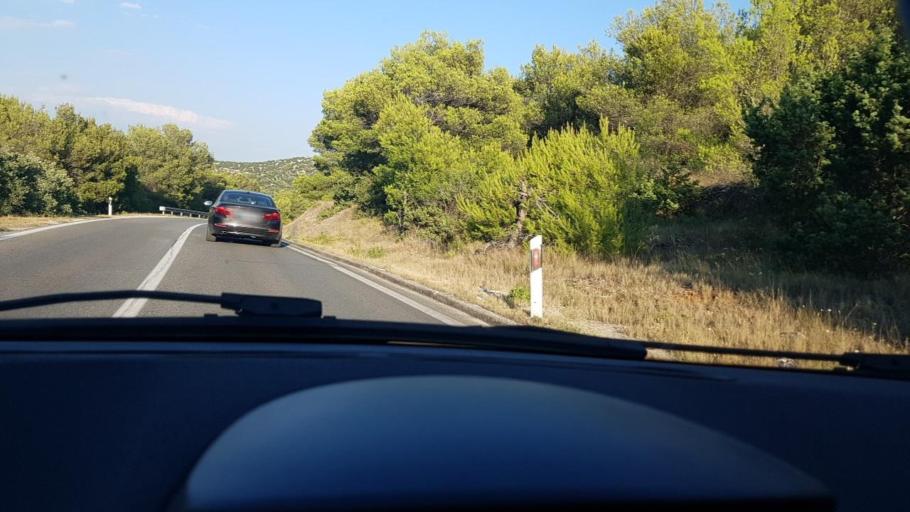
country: HR
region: Sibensko-Kniniska
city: Murter
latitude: 43.7967
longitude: 15.6178
